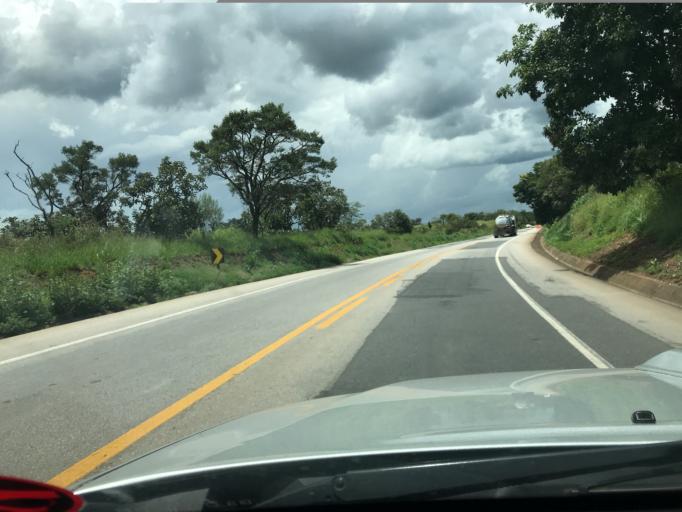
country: BR
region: Minas Gerais
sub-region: Ibia
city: Ibia
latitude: -19.5884
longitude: -46.4778
